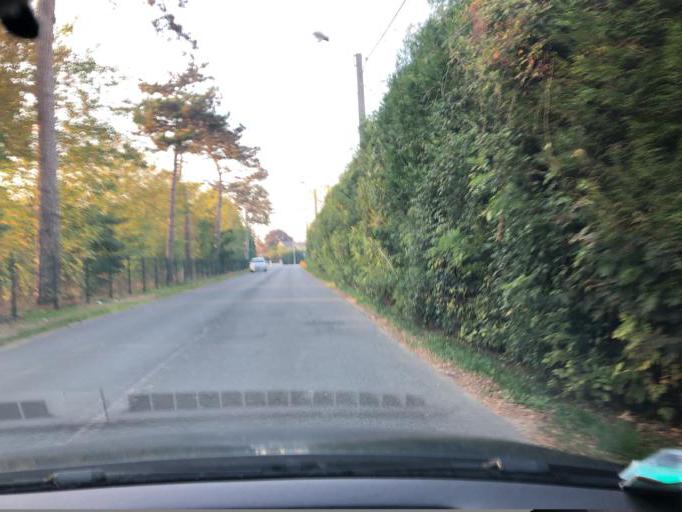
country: FR
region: Bourgogne
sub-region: Departement de l'Yonne
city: Saint-Clement
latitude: 48.2129
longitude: 3.2929
